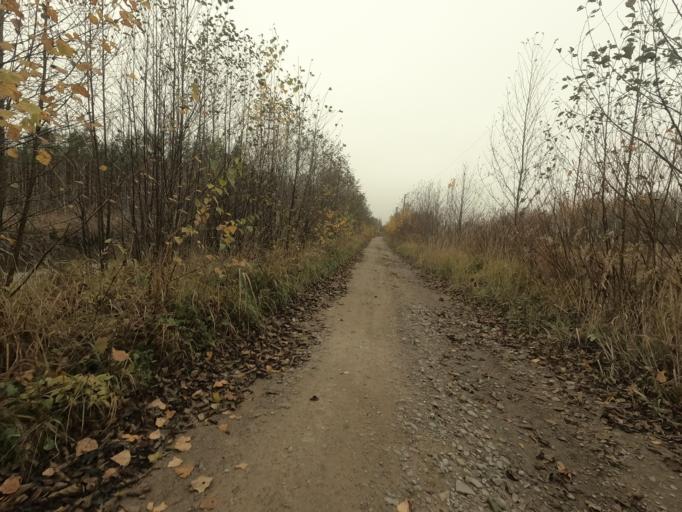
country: RU
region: Leningrad
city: Pavlovo
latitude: 59.7686
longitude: 30.9287
